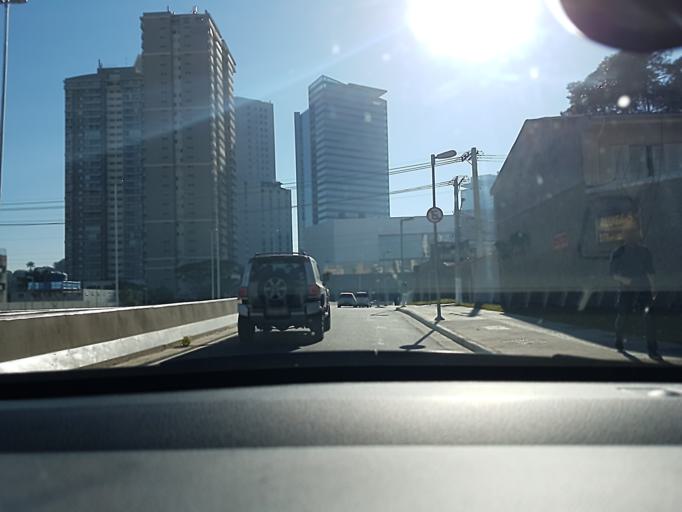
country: BR
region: Sao Paulo
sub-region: Taboao Da Serra
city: Taboao da Serra
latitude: -23.6277
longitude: -46.7074
